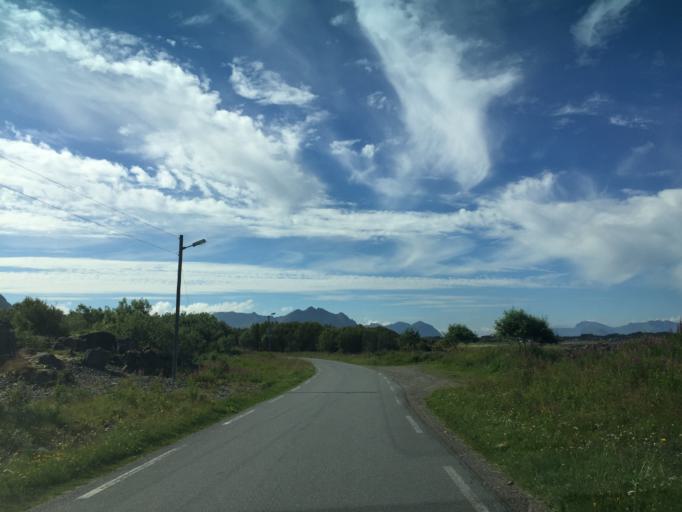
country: NO
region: Nordland
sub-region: Vagan
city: Svolvaer
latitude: 68.3999
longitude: 14.4991
